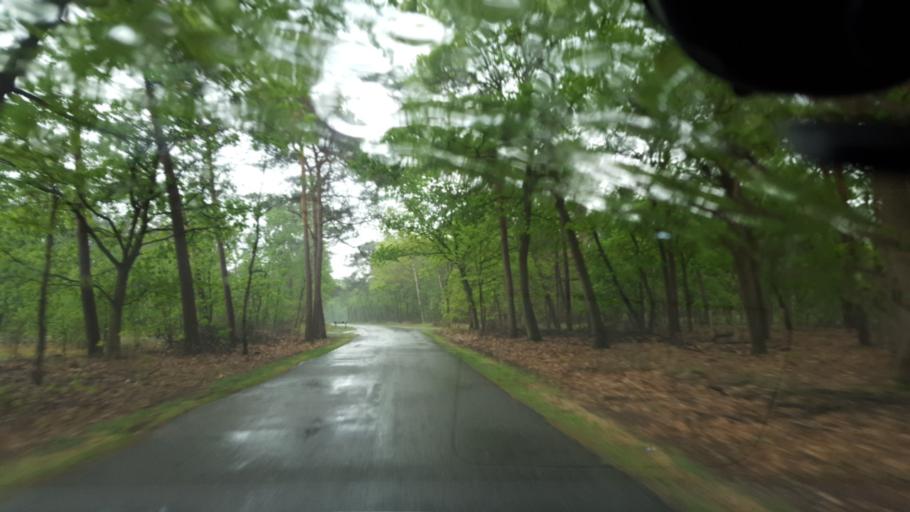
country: NL
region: North Brabant
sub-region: Gemeente Someren
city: Someren
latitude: 51.3950
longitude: 5.6707
